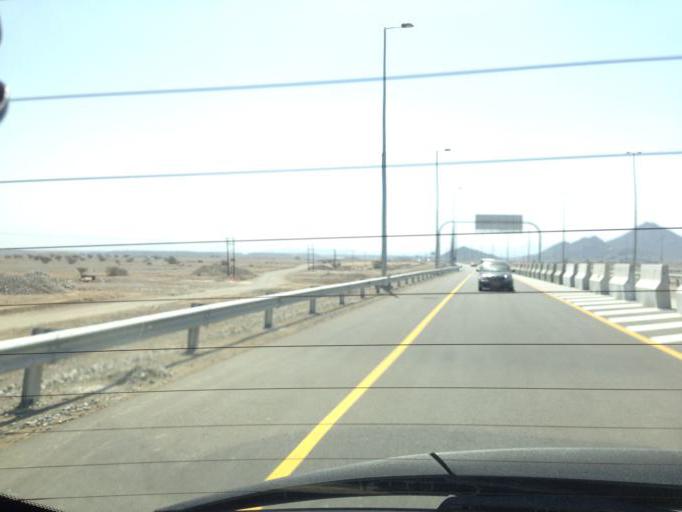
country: OM
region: Al Batinah
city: Rustaq
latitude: 23.5687
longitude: 57.4926
